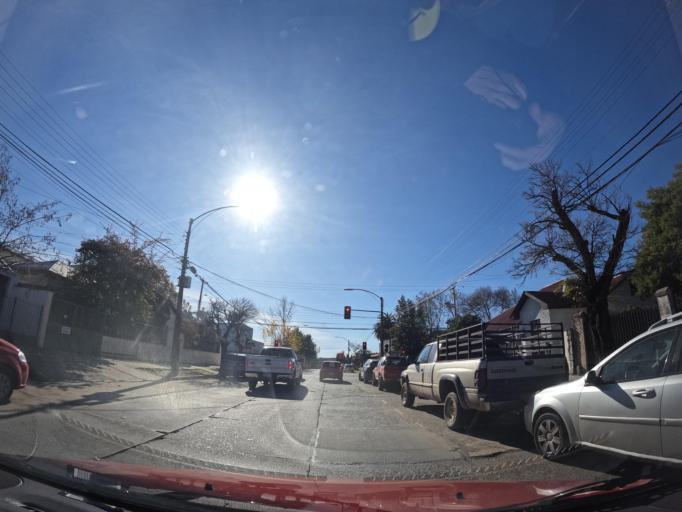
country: CL
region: Maule
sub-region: Provincia de Cauquenes
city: Cauquenes
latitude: -35.9645
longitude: -72.3145
